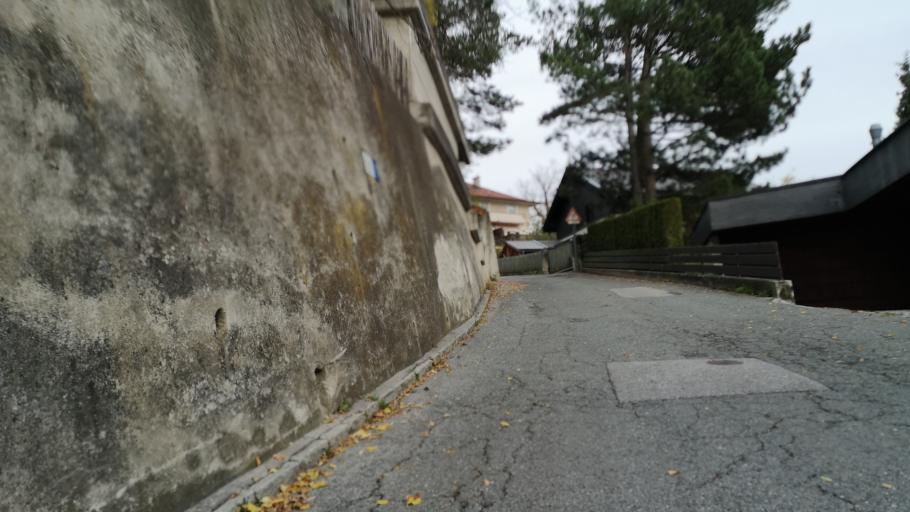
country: AT
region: Tyrol
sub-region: Innsbruck Stadt
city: Innsbruck
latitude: 47.2733
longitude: 11.3850
